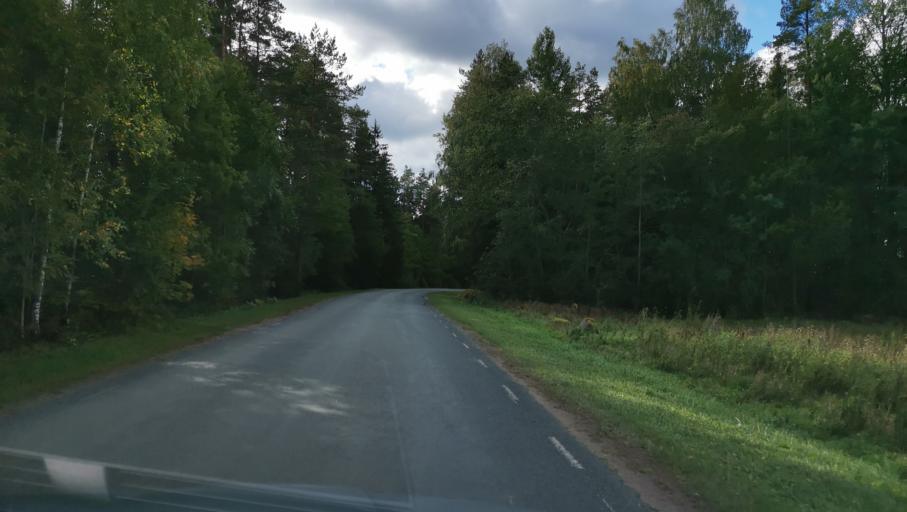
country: EE
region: Harju
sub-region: Nissi vald
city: Riisipere
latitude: 59.1325
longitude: 24.4871
